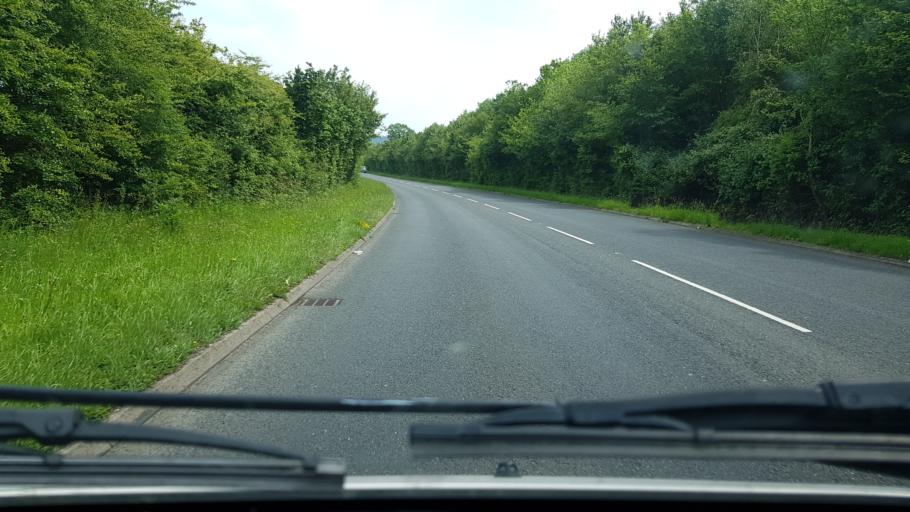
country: GB
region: England
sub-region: Worcestershire
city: Broadway
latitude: 52.0487
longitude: -1.8730
